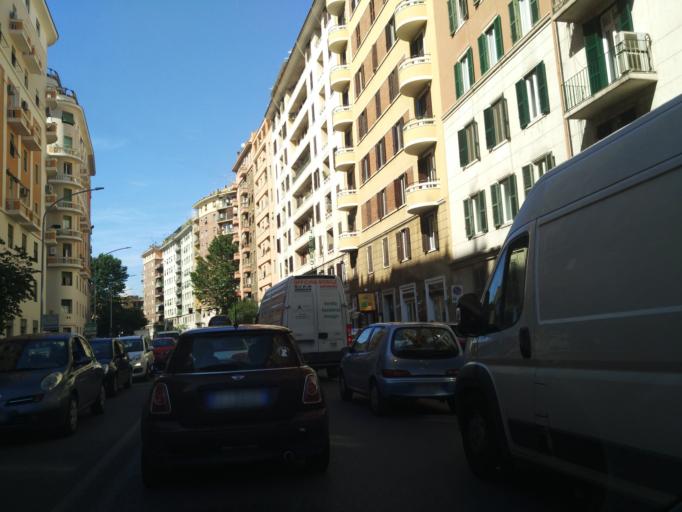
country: IT
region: Latium
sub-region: Citta metropolitana di Roma Capitale
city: Rome
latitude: 41.8757
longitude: 12.5076
